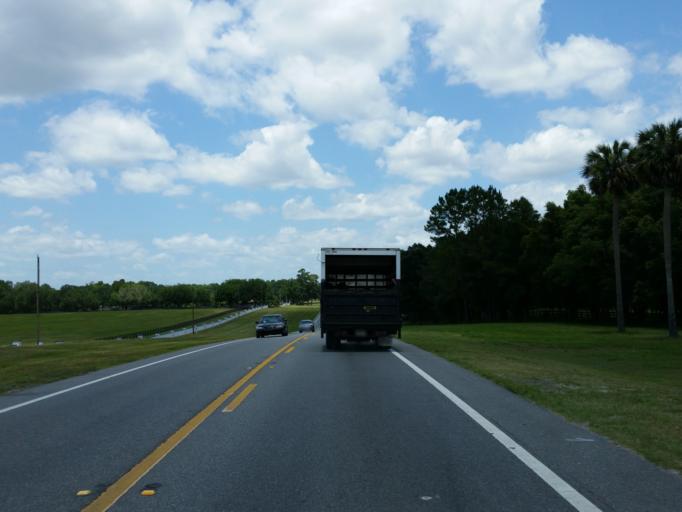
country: US
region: Florida
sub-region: Marion County
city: Belleview
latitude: 28.9941
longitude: -82.0413
